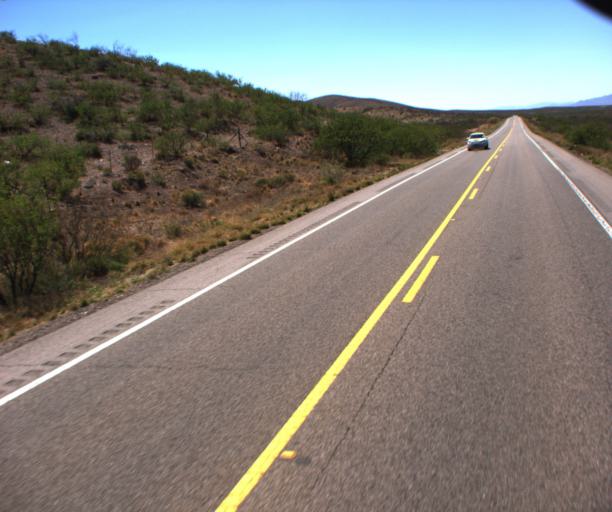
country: US
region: Arizona
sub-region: Cochise County
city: Douglas
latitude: 31.4765
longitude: -109.4485
